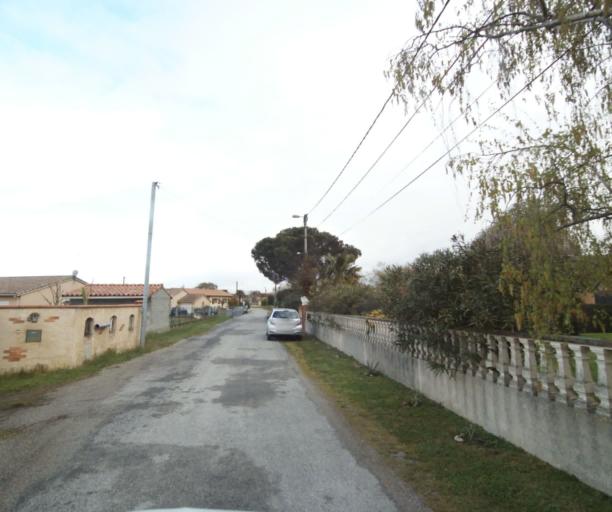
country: FR
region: Midi-Pyrenees
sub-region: Departement de l'Ariege
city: Saverdun
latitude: 43.2270
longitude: 1.5895
